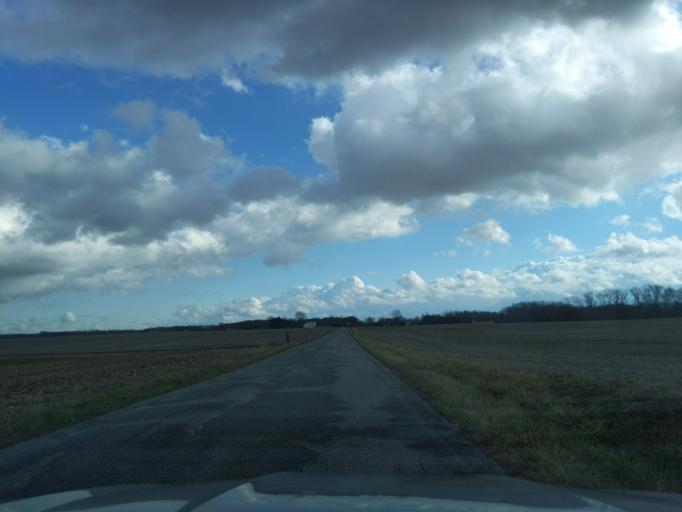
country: US
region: Indiana
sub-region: Decatur County
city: Greensburg
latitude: 39.4092
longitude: -85.5296
